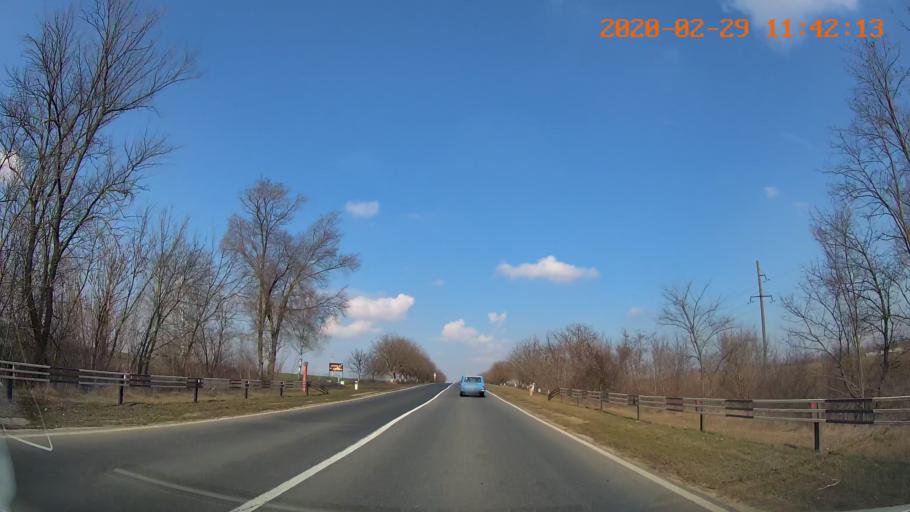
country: MD
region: Rezina
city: Saharna
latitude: 47.6809
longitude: 29.0138
